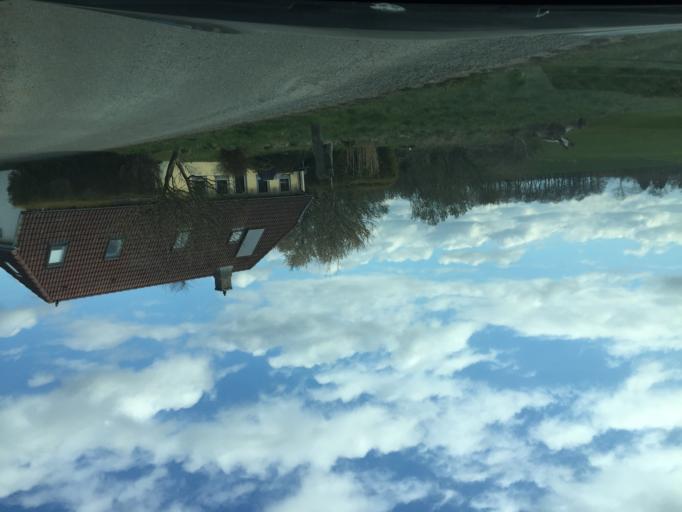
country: DK
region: South Denmark
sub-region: Faaborg-Midtfyn Kommune
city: Arslev
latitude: 55.3255
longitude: 10.4600
